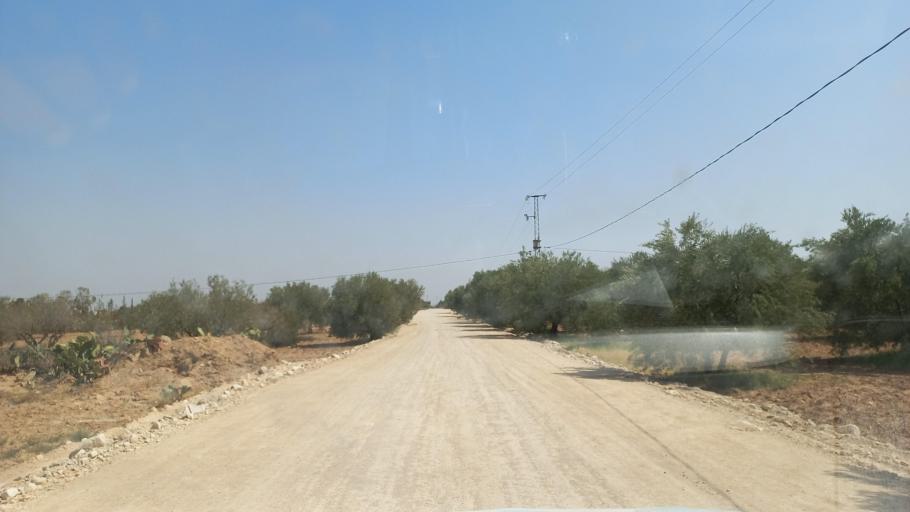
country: TN
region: Al Qasrayn
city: Kasserine
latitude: 35.2583
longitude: 9.0125
